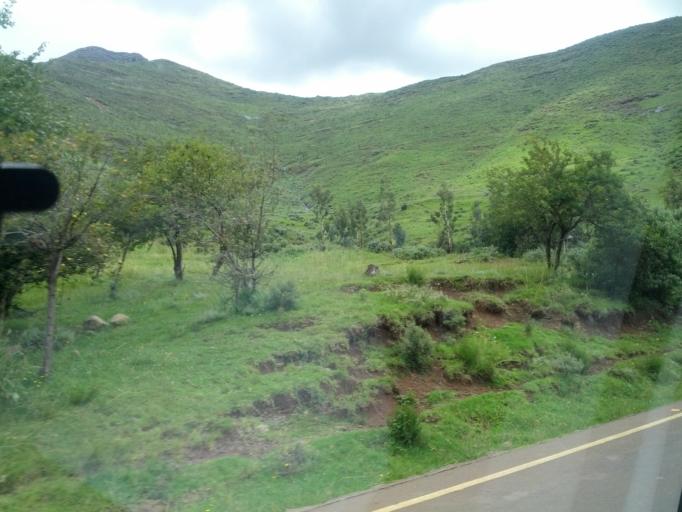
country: LS
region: Butha-Buthe
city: Butha-Buthe
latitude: -29.0487
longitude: 28.3256
